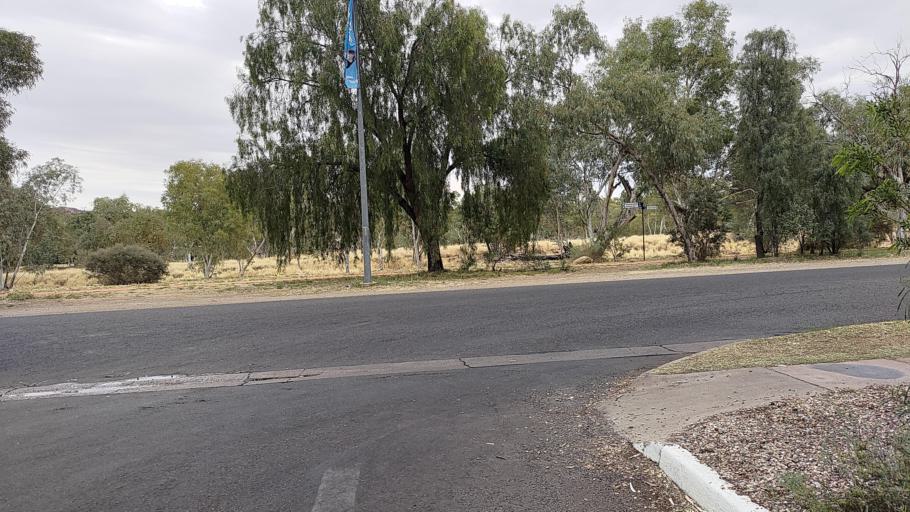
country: AU
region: Northern Territory
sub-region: Alice Springs
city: Alice Springs
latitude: -23.7142
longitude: 133.8793
